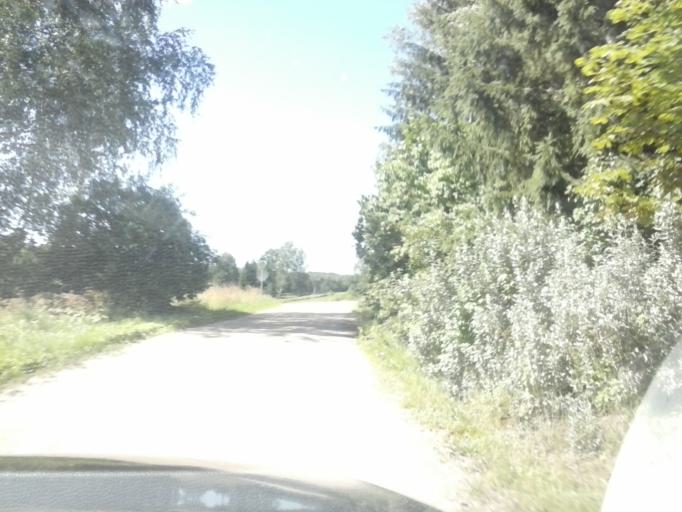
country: LV
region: Apes Novads
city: Ape
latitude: 57.5736
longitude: 26.6660
